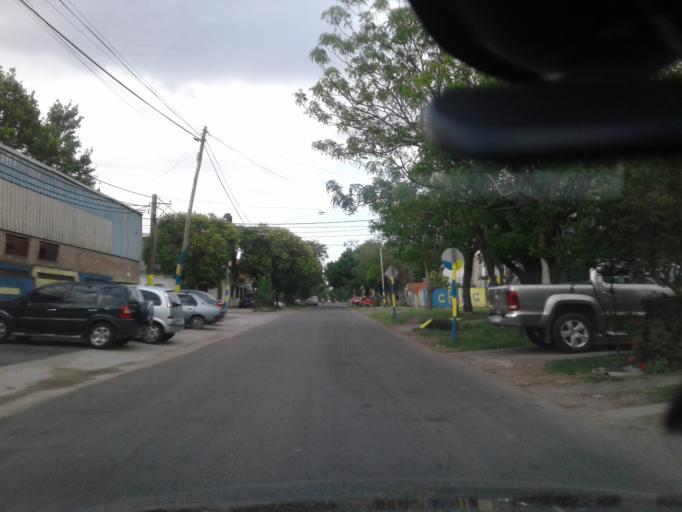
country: AR
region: Santa Fe
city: Granadero Baigorria
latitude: -32.8917
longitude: -60.7203
